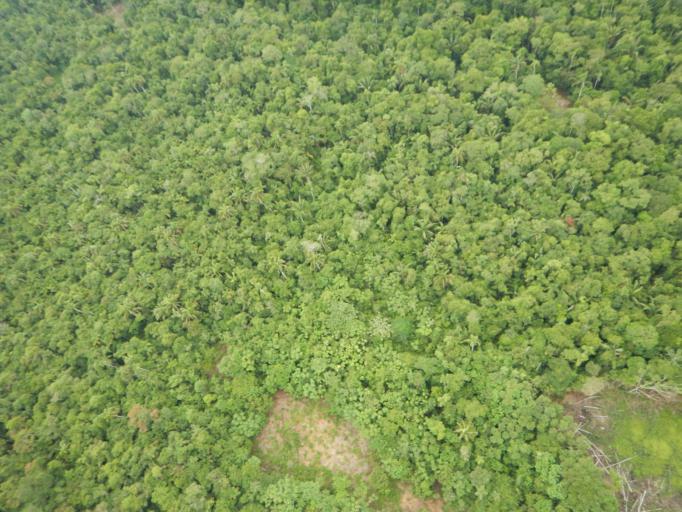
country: BO
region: Cochabamba
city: Chimore
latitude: -16.9147
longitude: -64.9240
